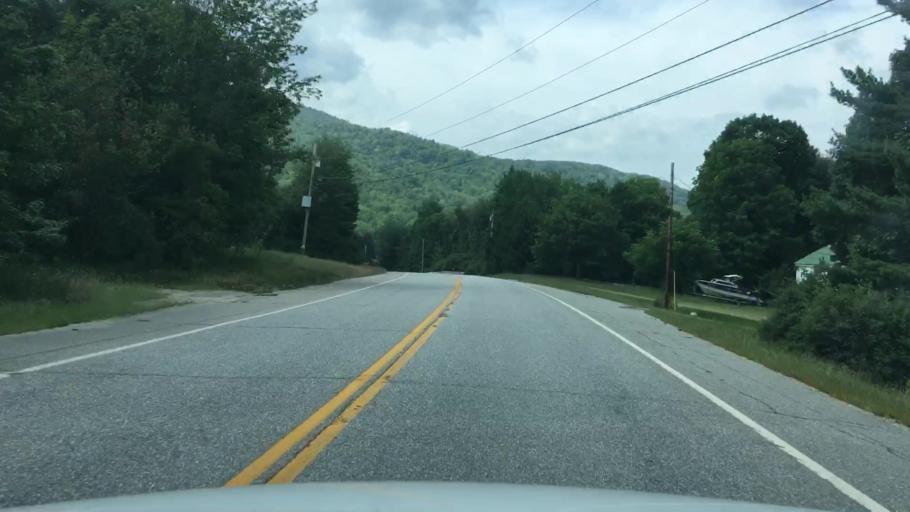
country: US
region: Maine
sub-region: Oxford County
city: Rumford
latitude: 44.5482
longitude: -70.7013
